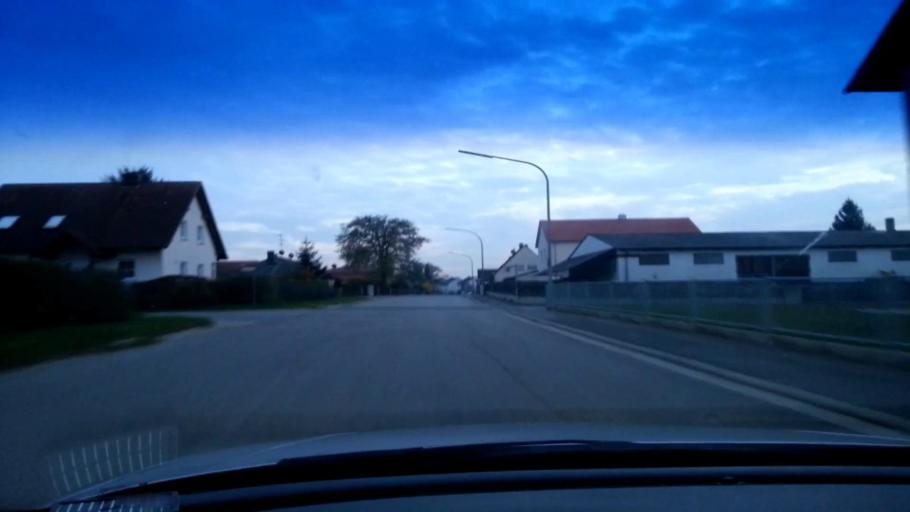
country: DE
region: Bavaria
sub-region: Upper Franconia
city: Breitengussbach
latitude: 49.9693
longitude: 10.8891
